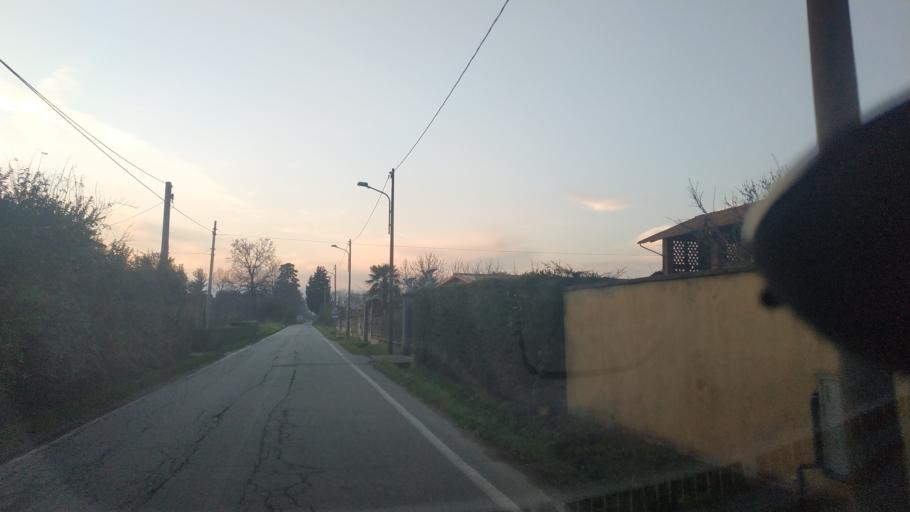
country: IT
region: Piedmont
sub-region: Provincia di Torino
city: Montanaro
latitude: 45.2665
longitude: 7.8758
